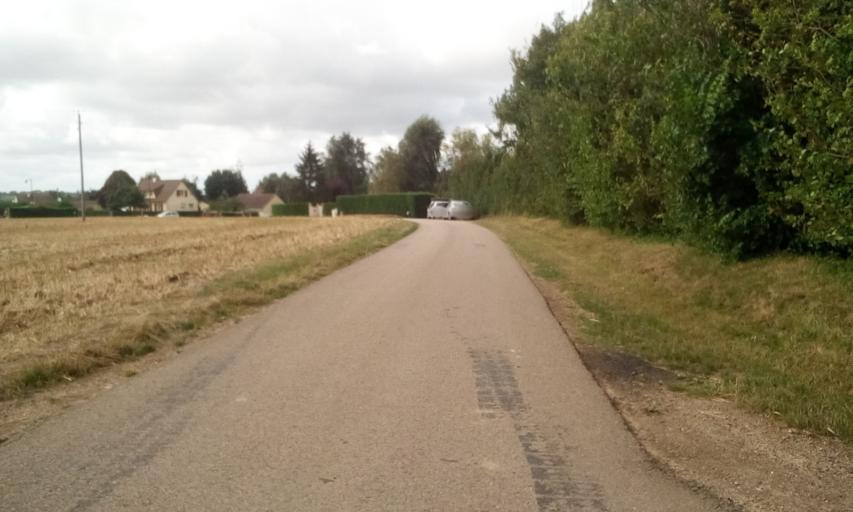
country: FR
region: Lower Normandy
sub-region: Departement du Calvados
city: Tilly-sur-Seulles
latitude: 49.2342
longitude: -0.6177
